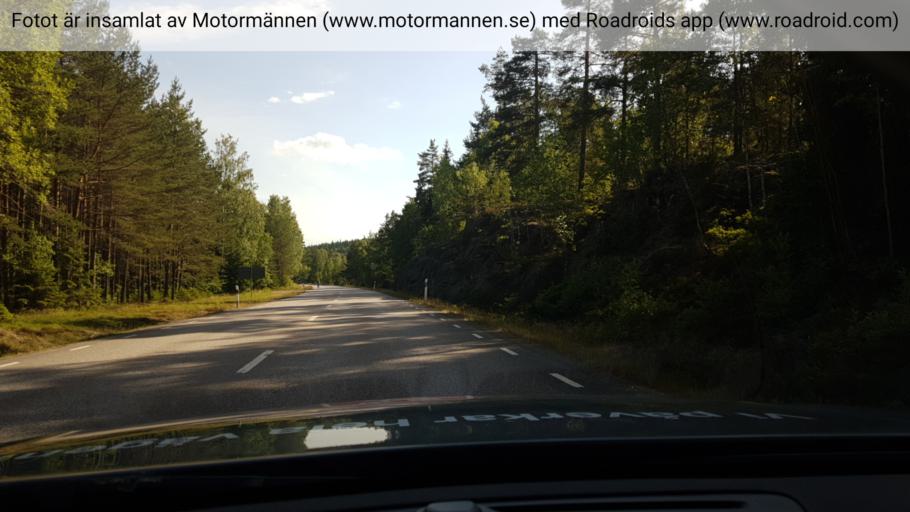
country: SE
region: Vaestra Goetaland
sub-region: Karlsborgs Kommun
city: Karlsborg
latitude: 58.6254
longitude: 14.5355
